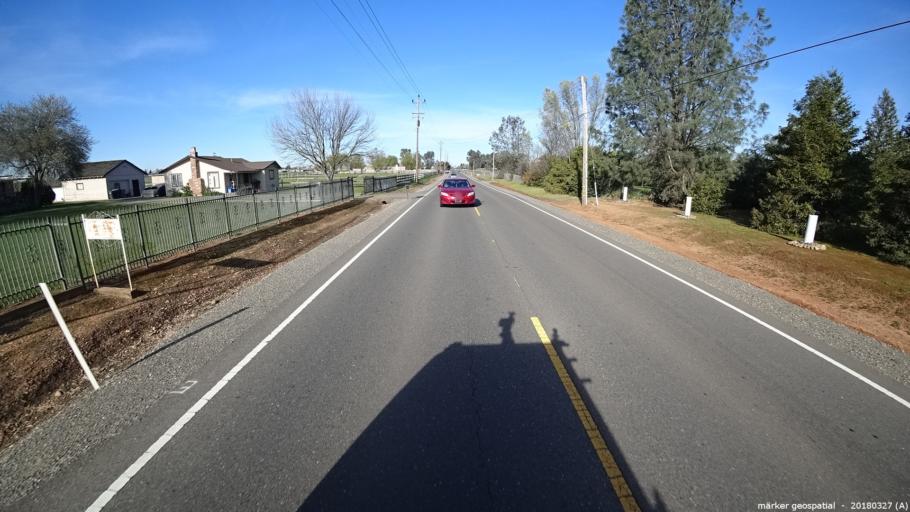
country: US
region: California
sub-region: Sacramento County
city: Vineyard
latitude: 38.4964
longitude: -121.3284
